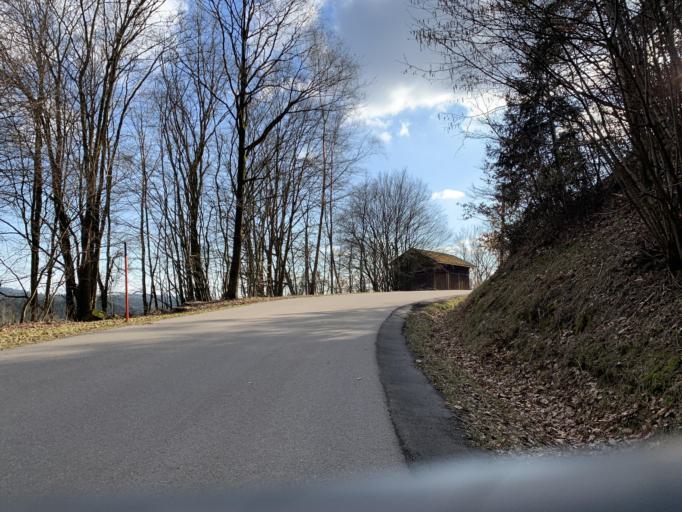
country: DE
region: Bavaria
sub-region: Upper Palatinate
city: Thanstein
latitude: 49.3797
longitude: 12.4515
